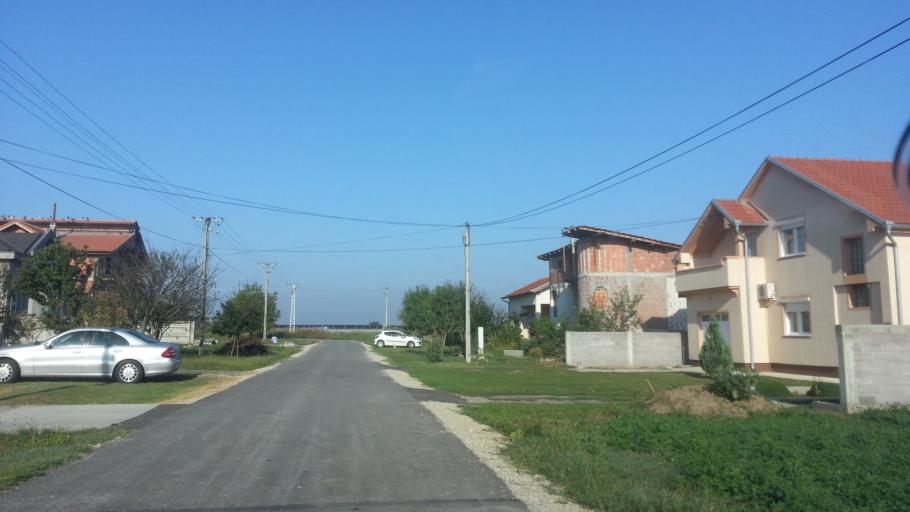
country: RS
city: Stari Banovci
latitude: 44.9871
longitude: 20.2693
